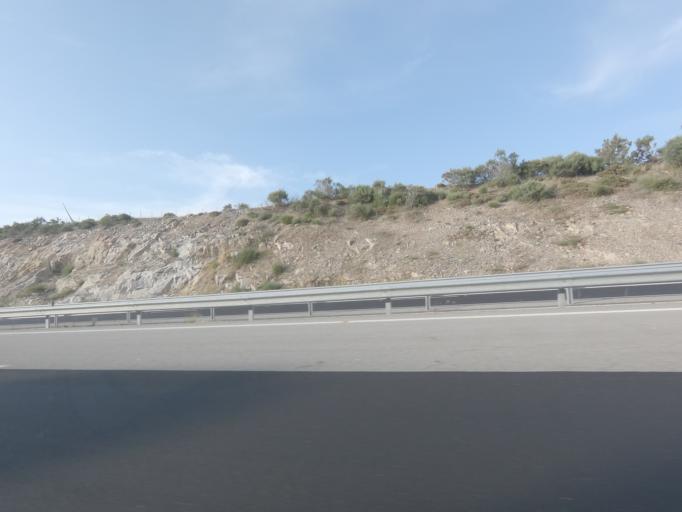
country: PT
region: Vila Real
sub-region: Vila Pouca de Aguiar
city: Vila Pouca de Aguiar
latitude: 41.4403
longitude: -7.6427
